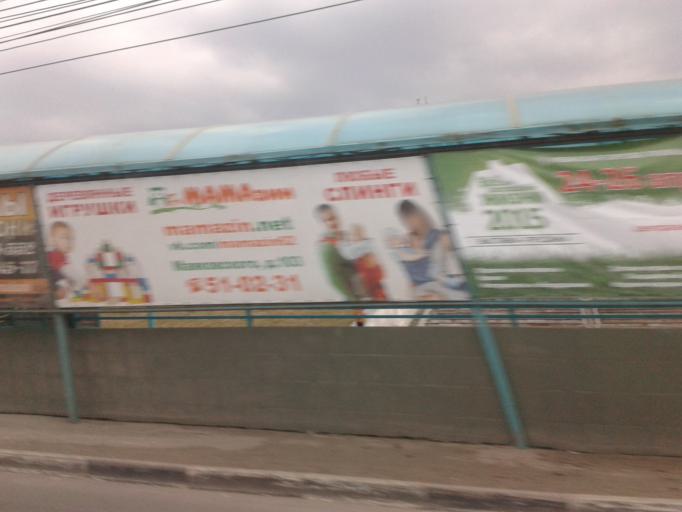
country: RU
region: Rjazan
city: Ryazan'
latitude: 54.6324
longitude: 39.6990
